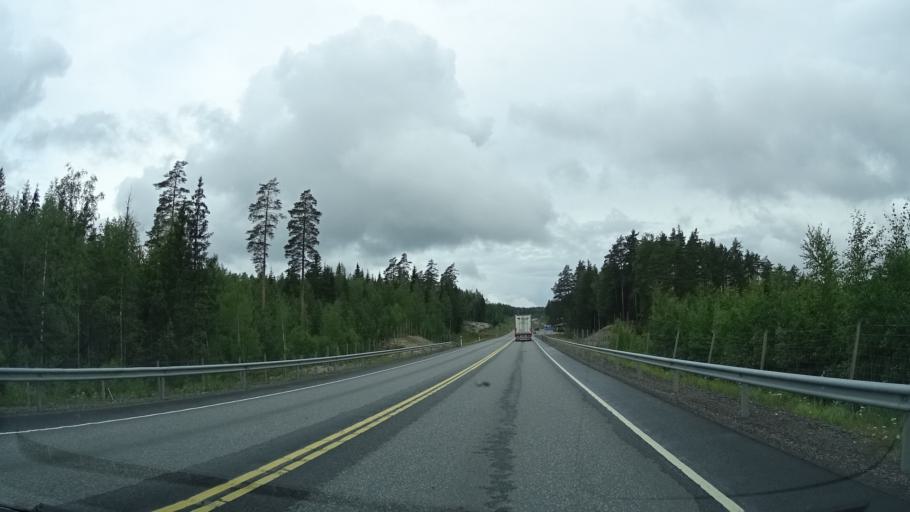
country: FI
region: Uusimaa
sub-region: Helsinki
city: Karkkila
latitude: 60.5899
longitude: 24.1124
